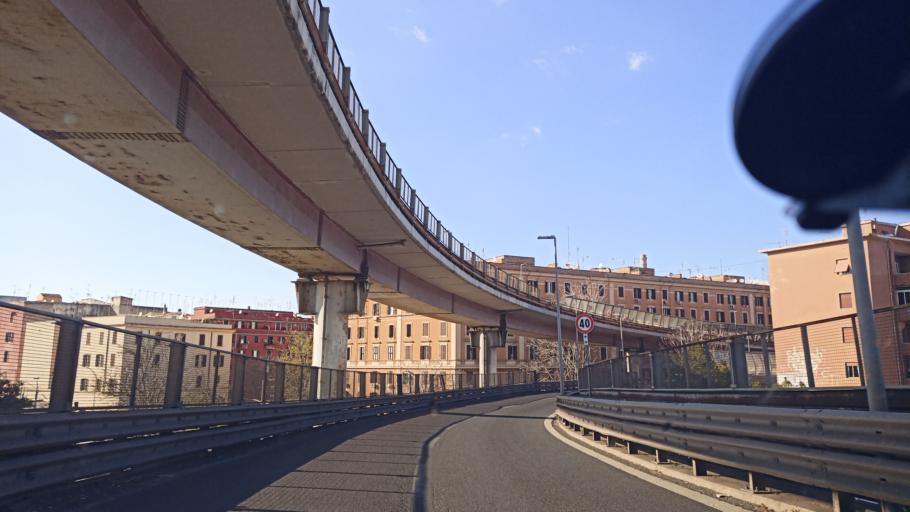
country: IT
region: Latium
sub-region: Citta metropolitana di Roma Capitale
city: Rome
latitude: 41.8939
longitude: 12.5177
